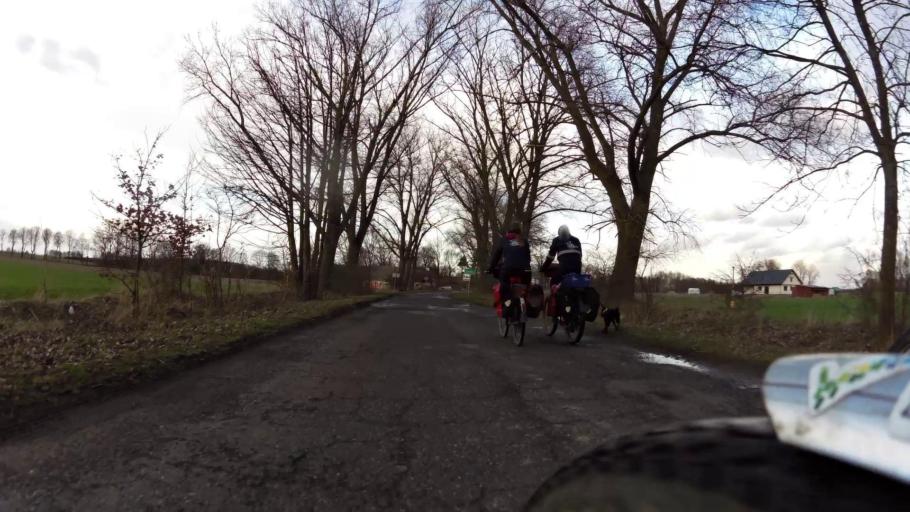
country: PL
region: West Pomeranian Voivodeship
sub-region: Powiat kamienski
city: Kamien Pomorski
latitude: 53.9160
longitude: 14.7325
